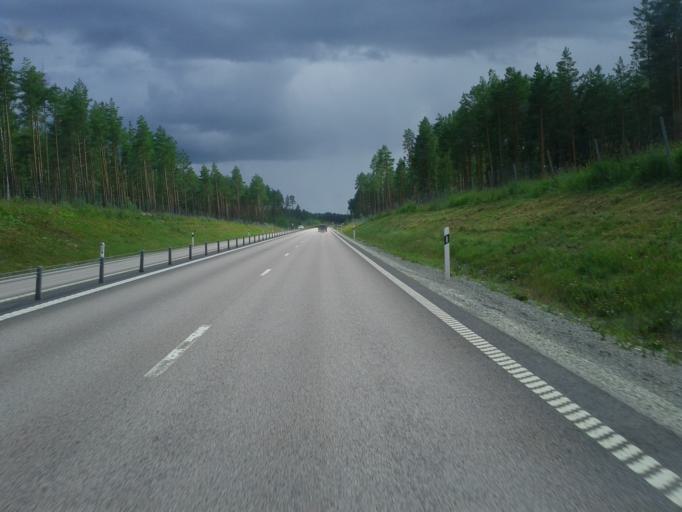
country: SE
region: Vaestmanland
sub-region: Sala Kommun
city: Sala
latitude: 59.9354
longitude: 16.5164
